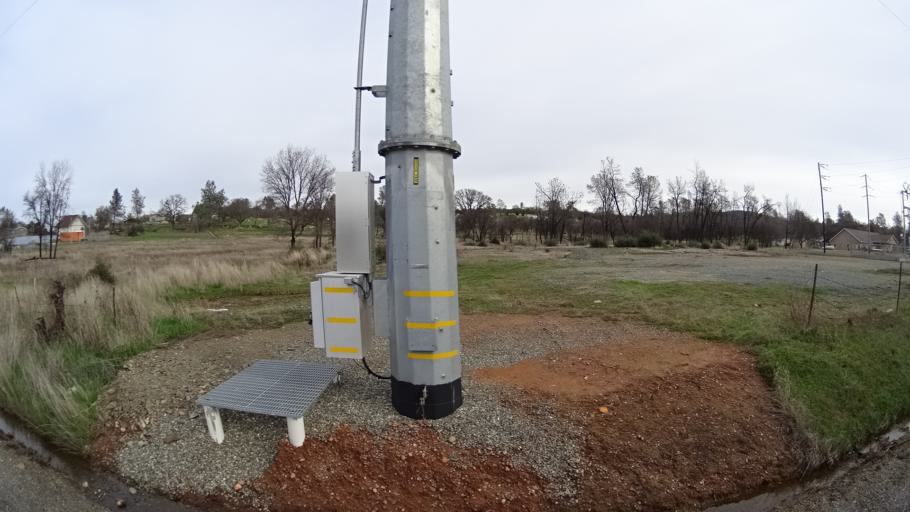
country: US
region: California
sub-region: Yuba County
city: Loma Rica
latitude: 39.3878
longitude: -121.4038
